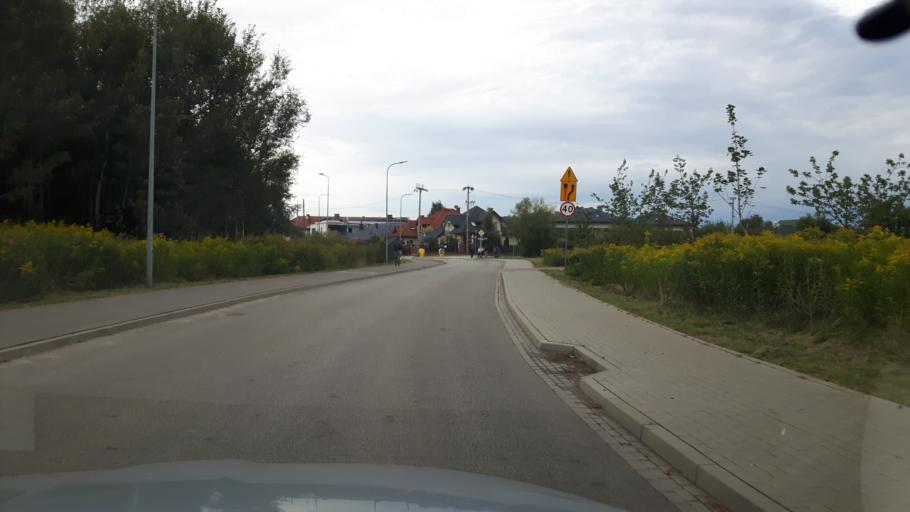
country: PL
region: Masovian Voivodeship
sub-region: Powiat wolominski
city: Marki
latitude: 52.3132
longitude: 21.0894
